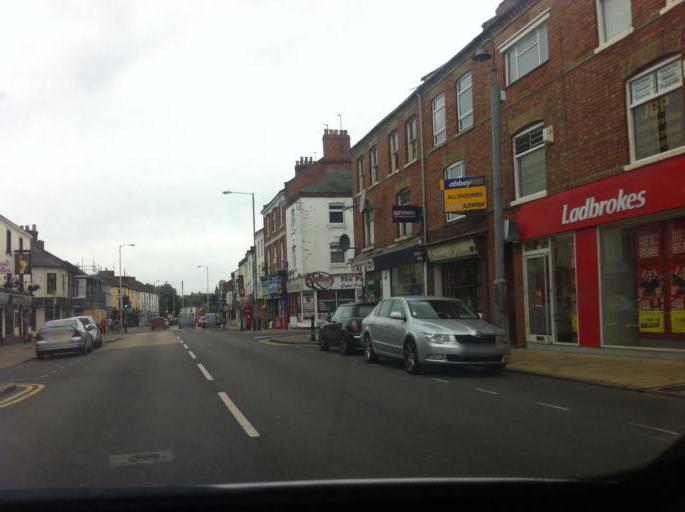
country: GB
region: England
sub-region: Northamptonshire
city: Northampton
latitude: 52.2417
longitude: -0.8788
